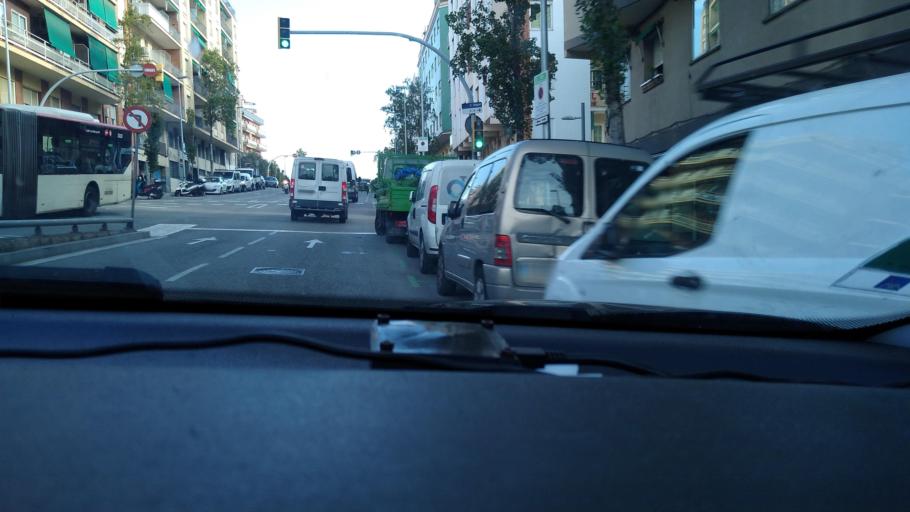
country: ES
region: Catalonia
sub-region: Provincia de Barcelona
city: Horta-Guinardo
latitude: 41.4166
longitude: 2.1744
